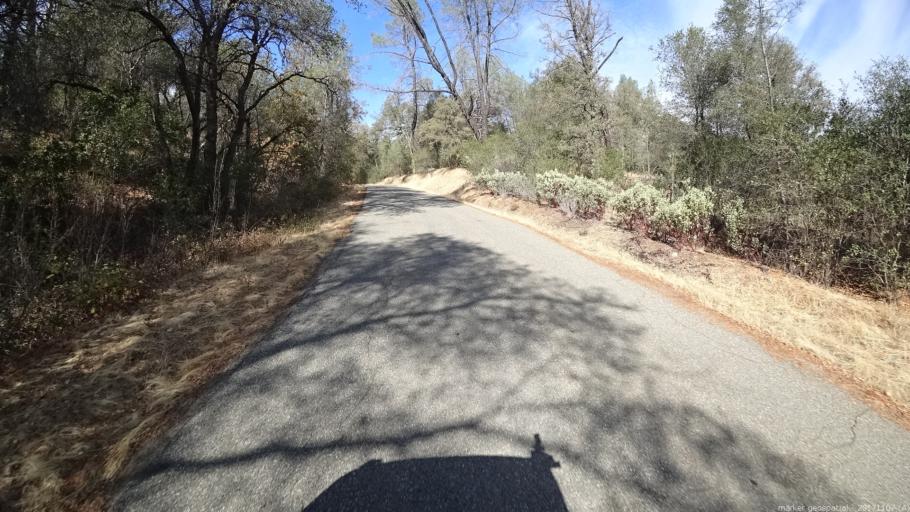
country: US
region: California
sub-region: Shasta County
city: Shasta
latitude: 40.5201
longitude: -122.5506
